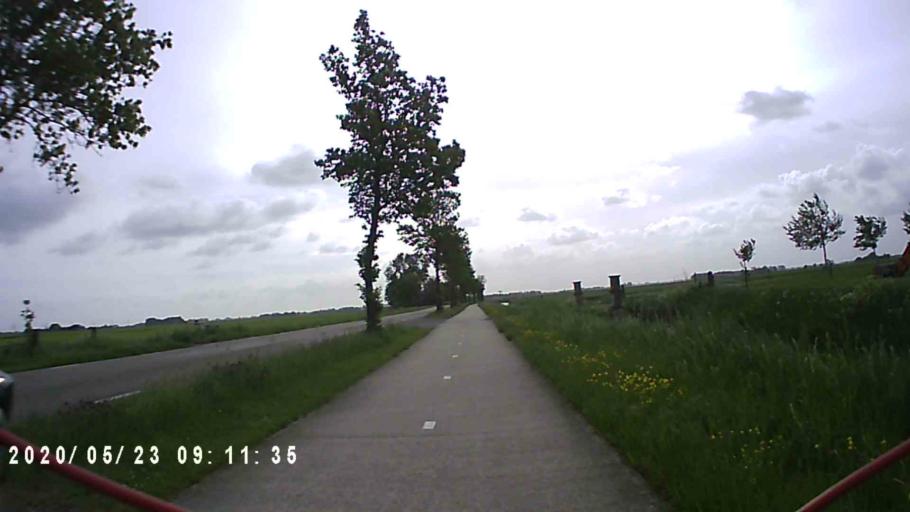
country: NL
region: Groningen
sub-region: Gemeente Bedum
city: Bedum
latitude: 53.3016
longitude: 6.6176
